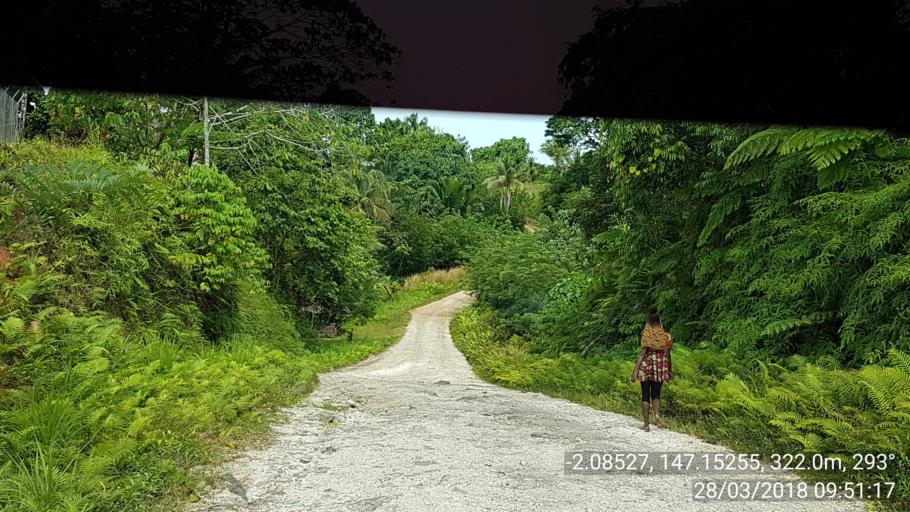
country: PG
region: Manus
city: Lorengau
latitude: -2.0853
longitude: 147.1525
